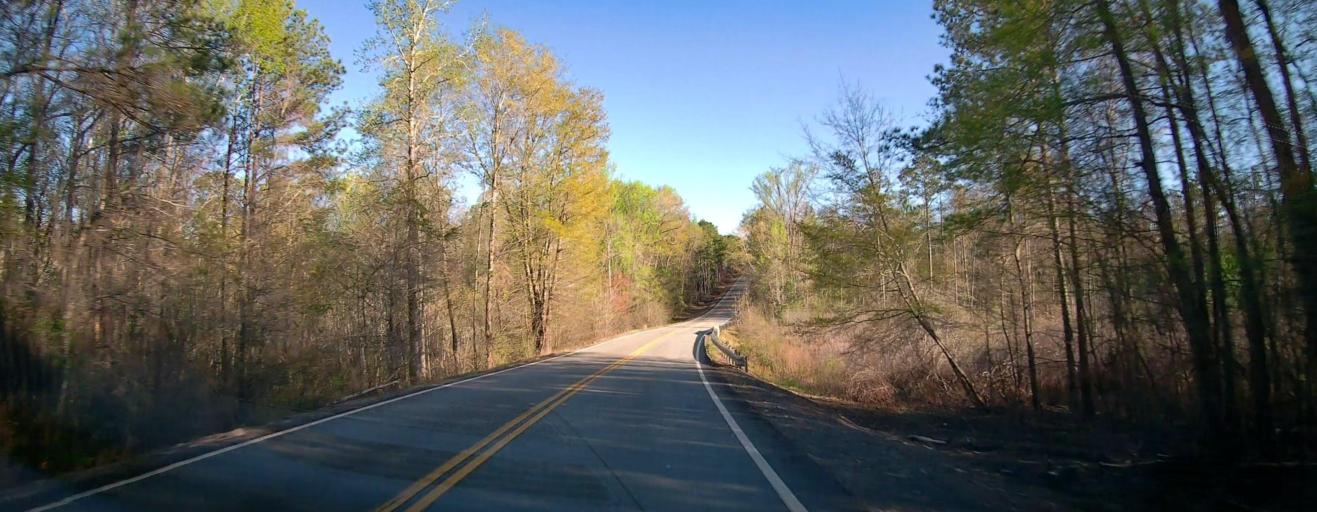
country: US
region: Georgia
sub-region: Wilkinson County
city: Irwinton
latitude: 32.9247
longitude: -83.1325
